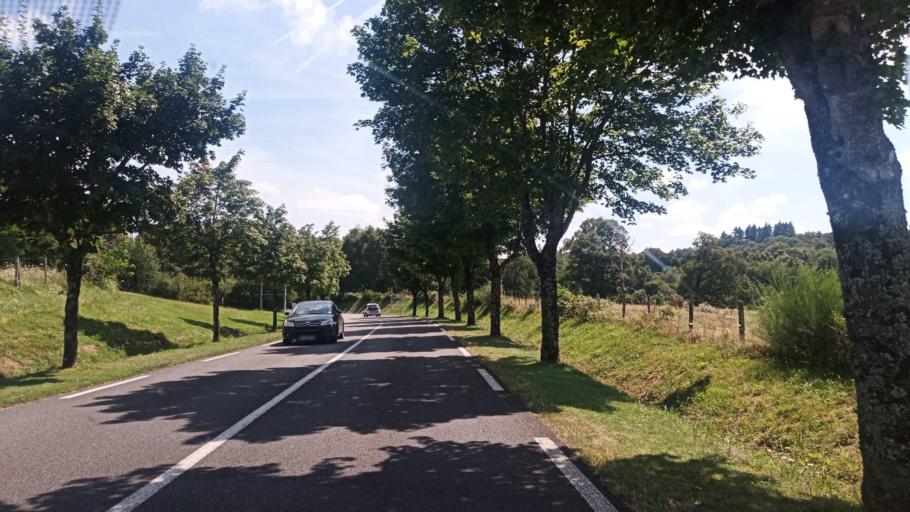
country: FR
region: Limousin
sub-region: Departement de la Haute-Vienne
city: Oradour-sur-Glane
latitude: 45.9274
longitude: 1.0379
